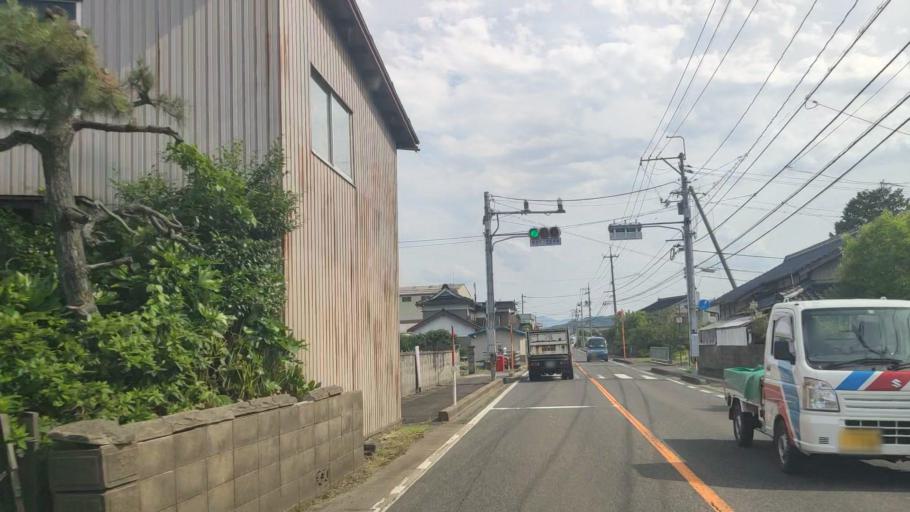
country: JP
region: Tottori
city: Tottori
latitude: 35.4671
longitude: 134.2038
